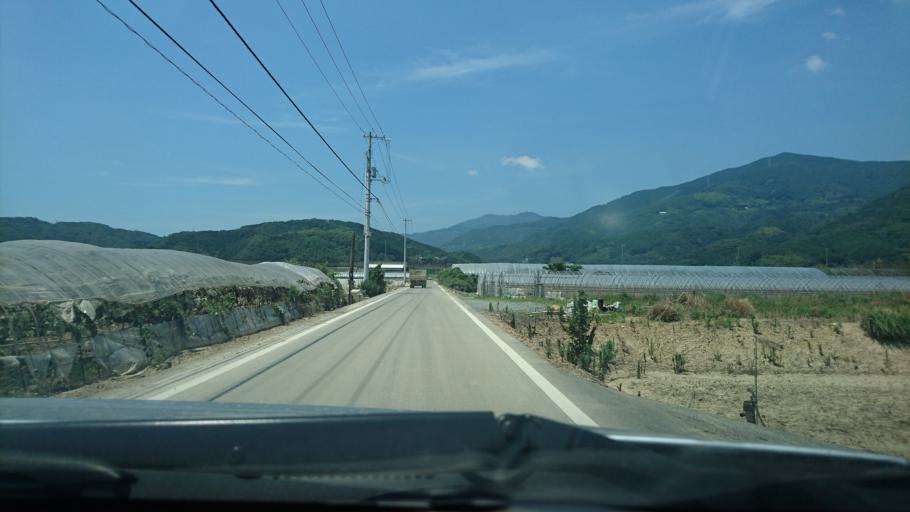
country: JP
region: Ehime
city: Ozu
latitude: 33.5313
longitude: 132.5682
